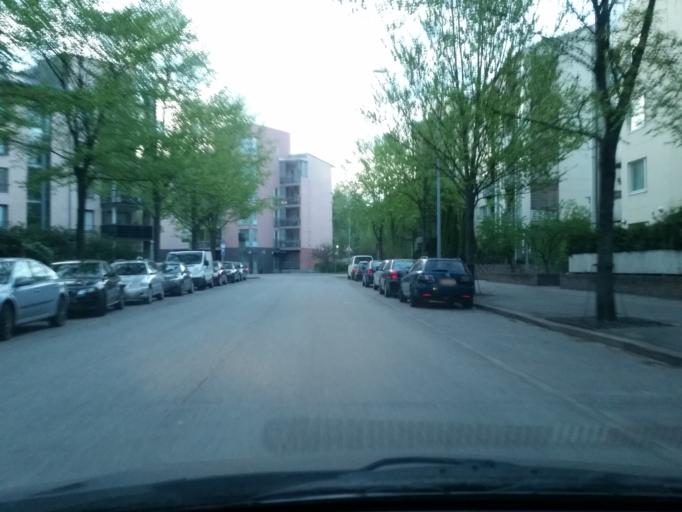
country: FI
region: Uusimaa
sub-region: Helsinki
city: Helsinki
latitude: 60.1898
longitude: 25.0365
